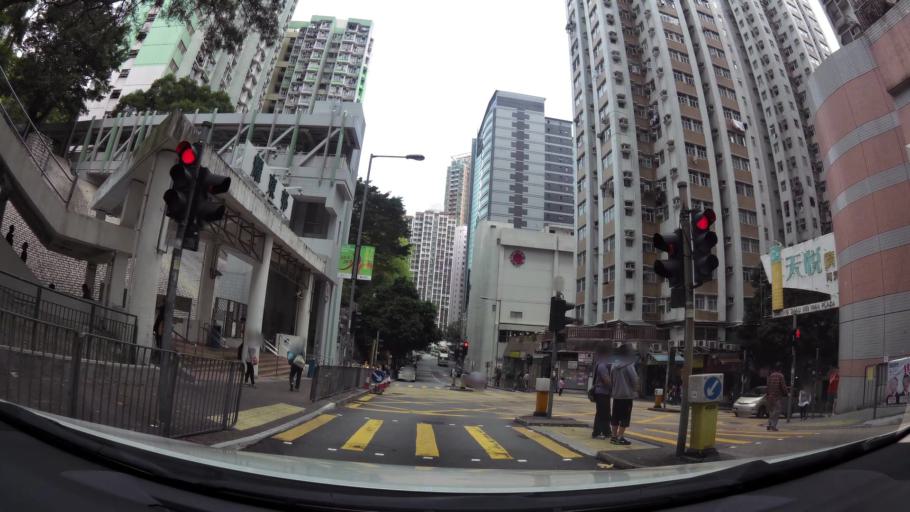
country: HK
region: Wanchai
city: Wan Chai
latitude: 22.2777
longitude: 114.2258
